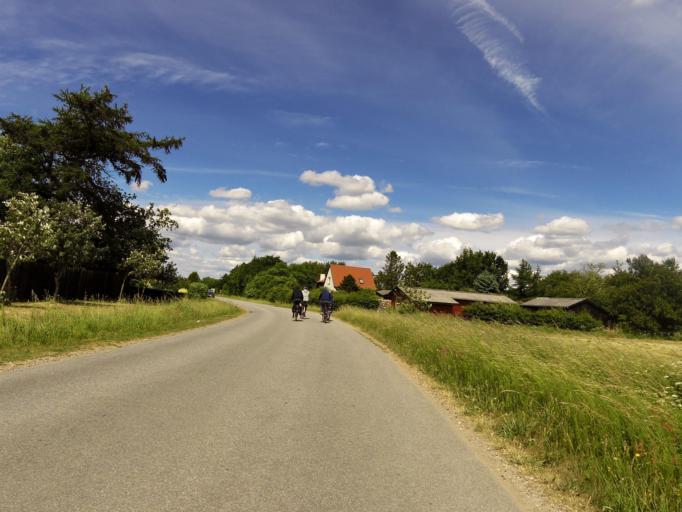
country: DK
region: South Denmark
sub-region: Esbjerg Kommune
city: Ribe
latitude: 55.3169
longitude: 8.7614
